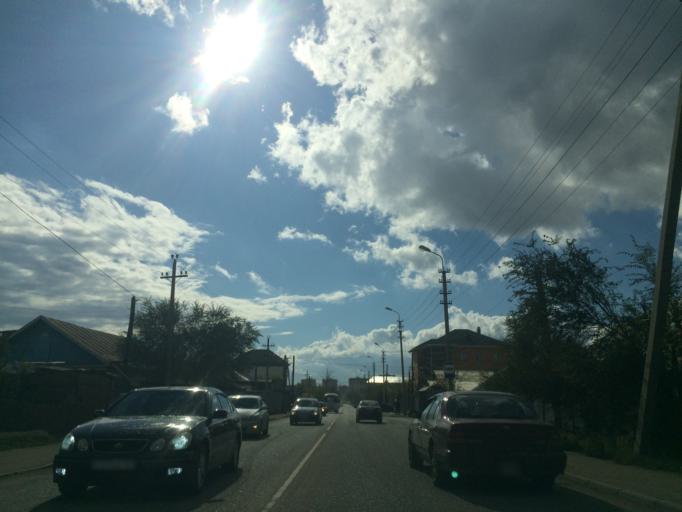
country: KZ
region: Astana Qalasy
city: Astana
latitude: 51.1902
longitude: 71.3860
